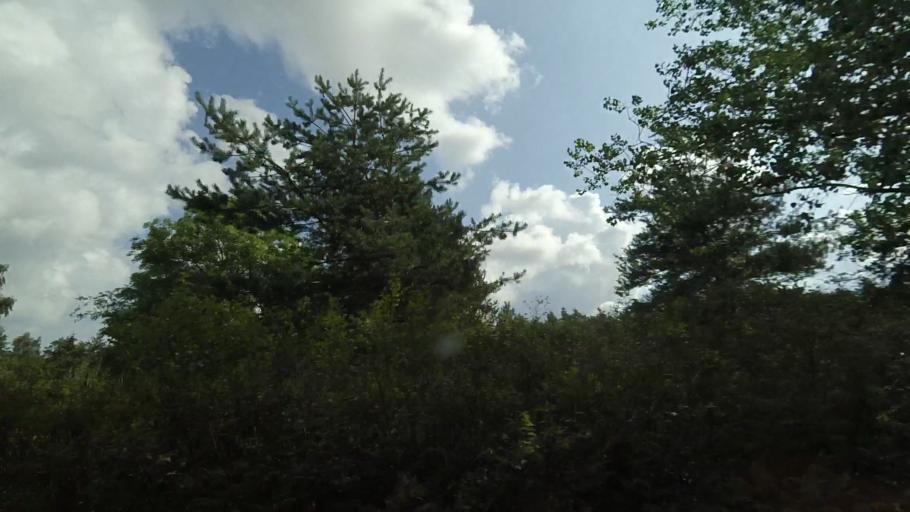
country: DK
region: Central Jutland
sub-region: Norddjurs Kommune
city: Allingabro
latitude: 56.5100
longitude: 10.3956
